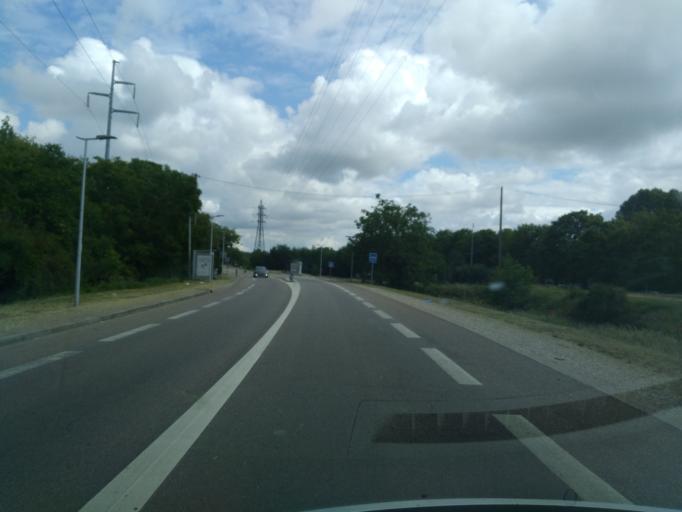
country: FR
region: Ile-de-France
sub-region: Departement des Yvelines
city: Carrieres-sous-Poissy
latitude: 48.9507
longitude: 2.0441
